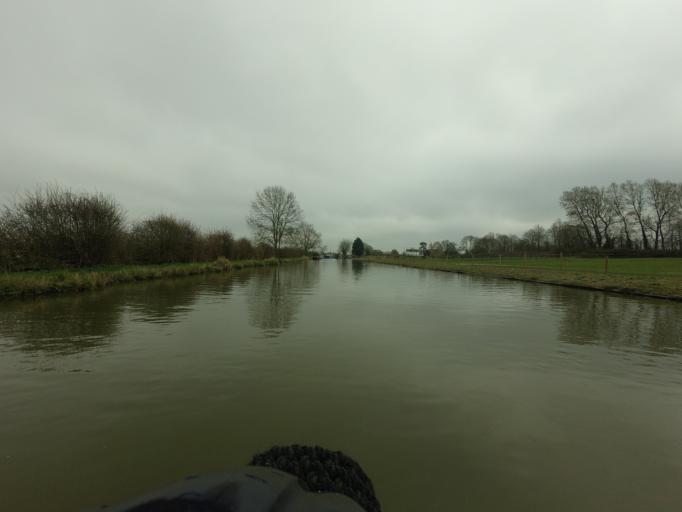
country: GB
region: England
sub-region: Central Bedfordshire
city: Leighton Buzzard
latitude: 51.8949
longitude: -0.6655
